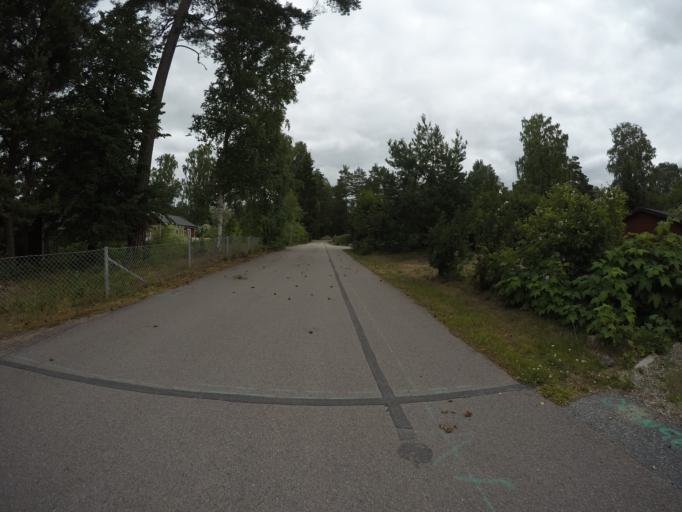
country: SE
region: Soedermanland
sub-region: Eskilstuna Kommun
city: Kvicksund
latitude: 59.4639
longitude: 16.3013
